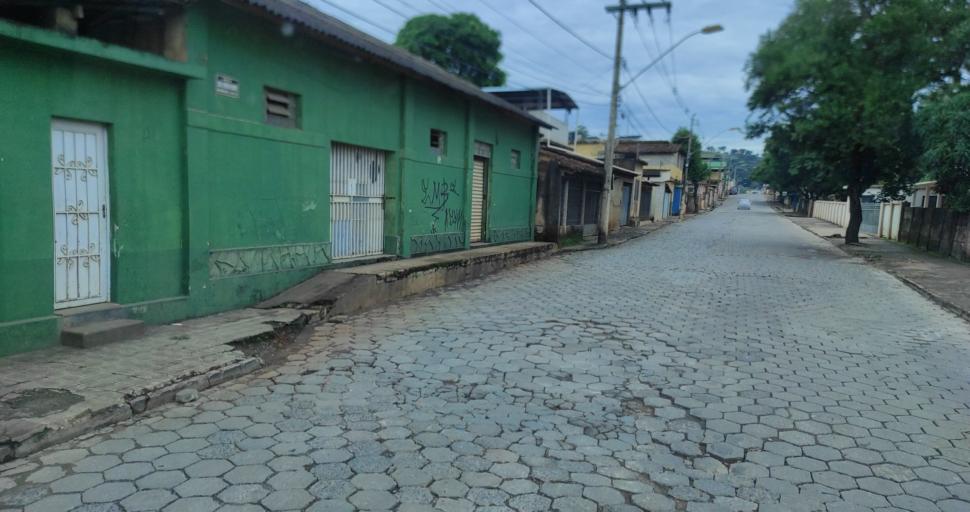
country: BR
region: Minas Gerais
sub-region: Arcos
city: Arcos
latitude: -20.3738
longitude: -45.6620
